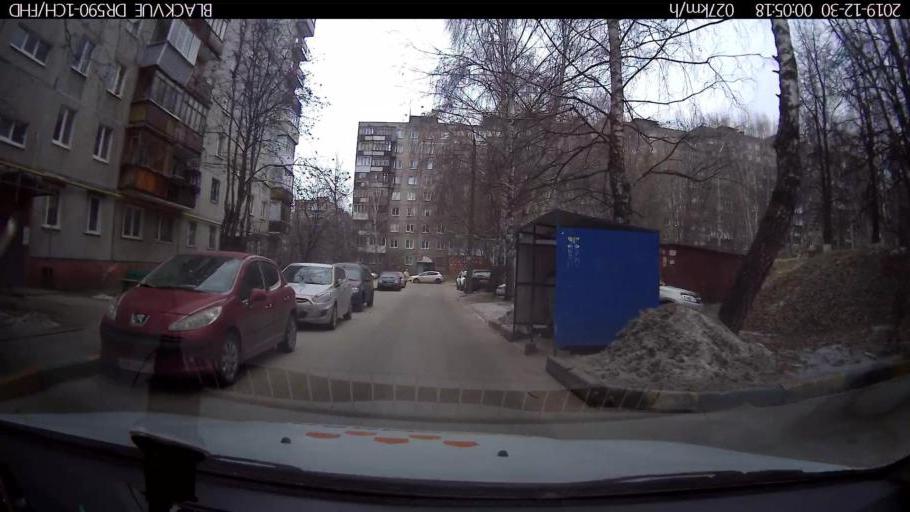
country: RU
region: Nizjnij Novgorod
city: Nizhniy Novgorod
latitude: 56.3145
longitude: 44.0481
